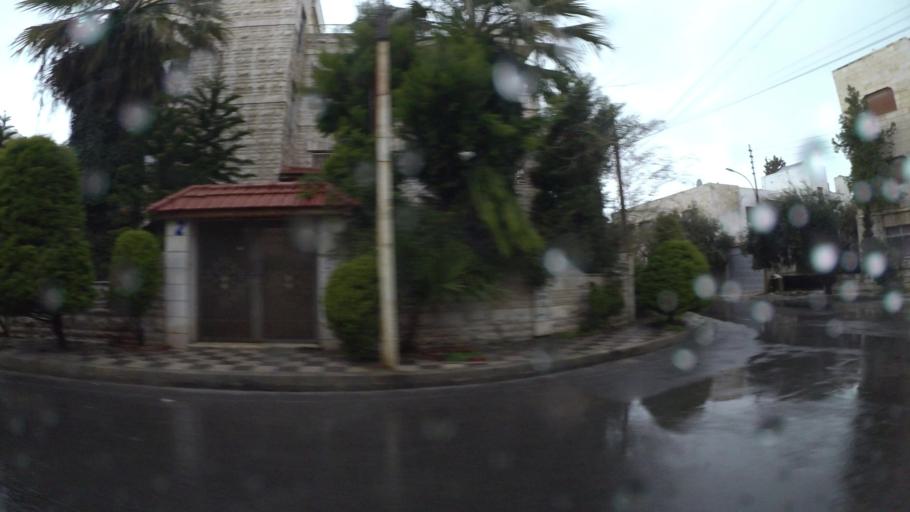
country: JO
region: Amman
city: Umm as Summaq
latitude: 31.8993
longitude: 35.8545
